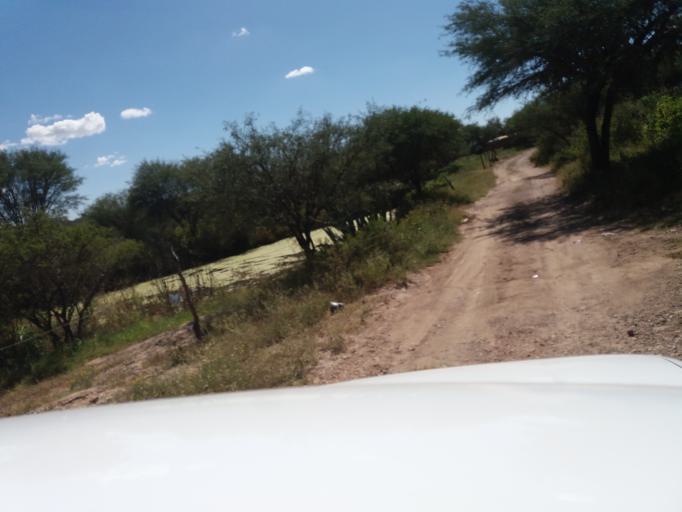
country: MX
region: Aguascalientes
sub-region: Aguascalientes
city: San Sebastian [Fraccionamiento]
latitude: 21.7752
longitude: -102.2287
